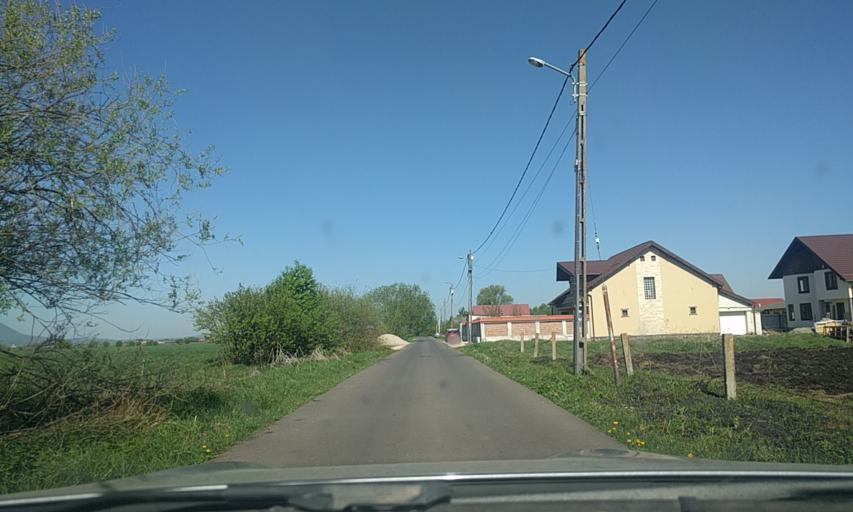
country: RO
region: Brasov
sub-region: Comuna Bod
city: Colonia Bod
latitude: 45.7172
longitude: 25.5709
